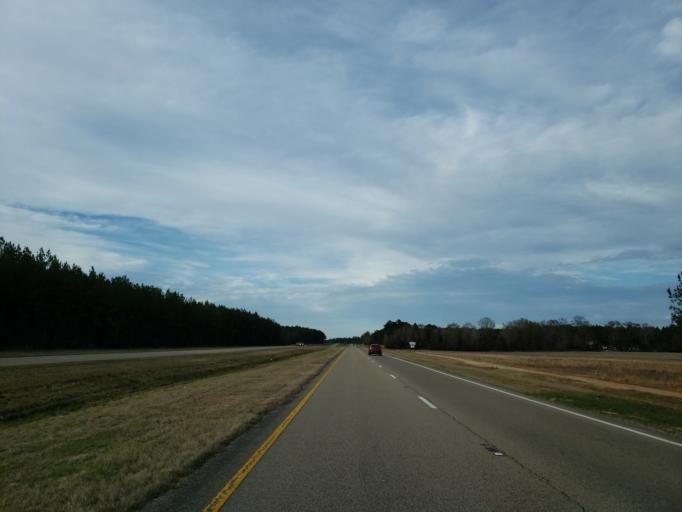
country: US
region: Mississippi
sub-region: Wayne County
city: Waynesboro
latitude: 31.6376
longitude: -88.5936
